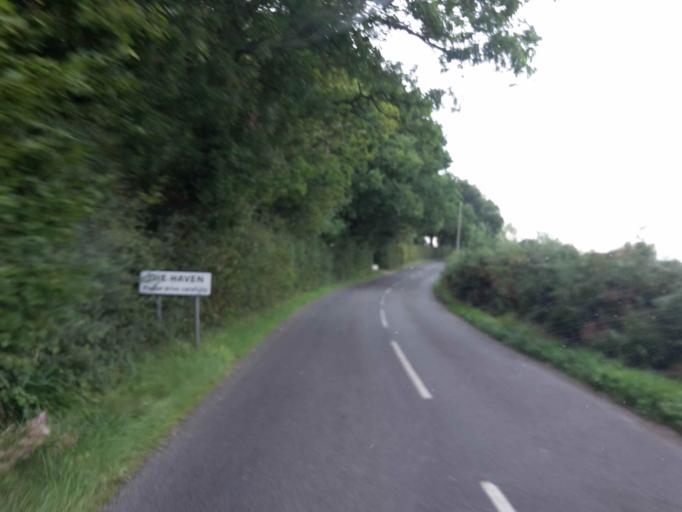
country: GB
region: England
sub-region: West Sussex
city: Rudgwick
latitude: 51.0686
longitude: -0.4473
